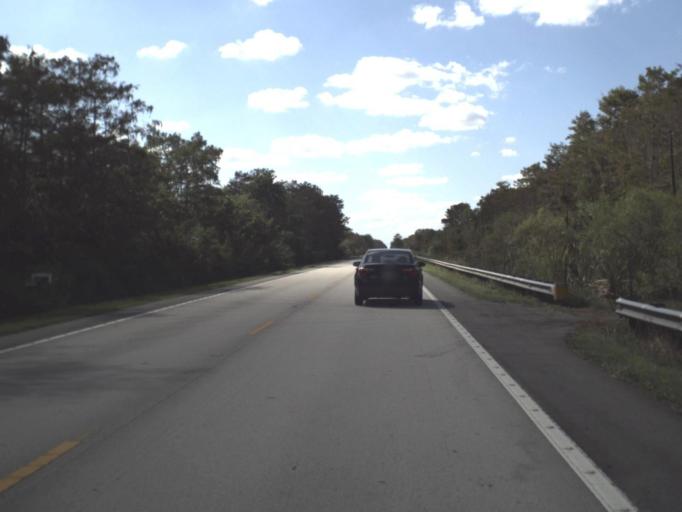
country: US
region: Florida
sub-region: Miami-Dade County
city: Kendall West
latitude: 25.8565
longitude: -81.0292
